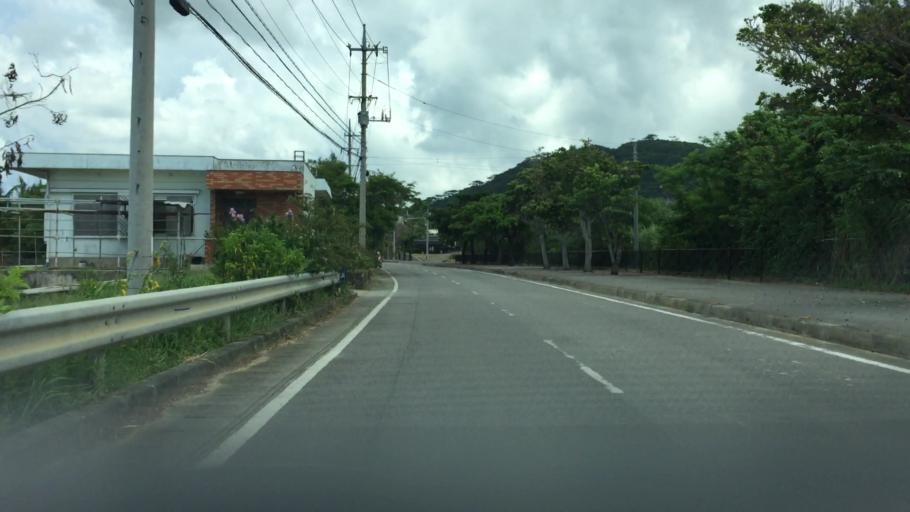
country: JP
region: Okinawa
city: Ishigaki
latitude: 24.3627
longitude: 124.1429
